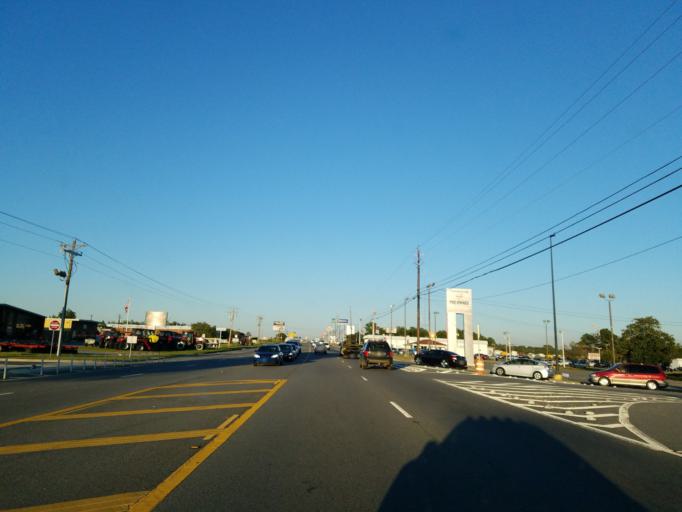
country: US
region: Georgia
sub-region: Tift County
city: Tifton
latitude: 31.4457
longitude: -83.5430
